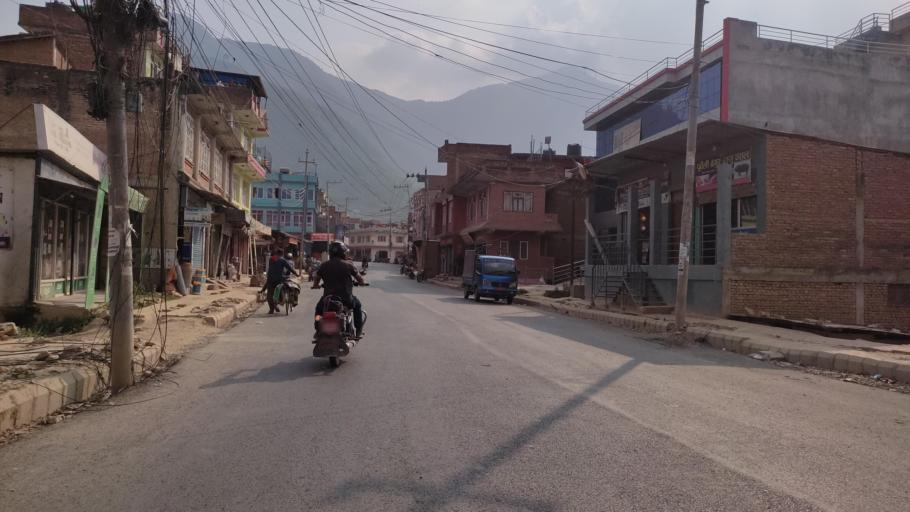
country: NP
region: Central Region
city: Kirtipur
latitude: 27.6667
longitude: 85.2660
